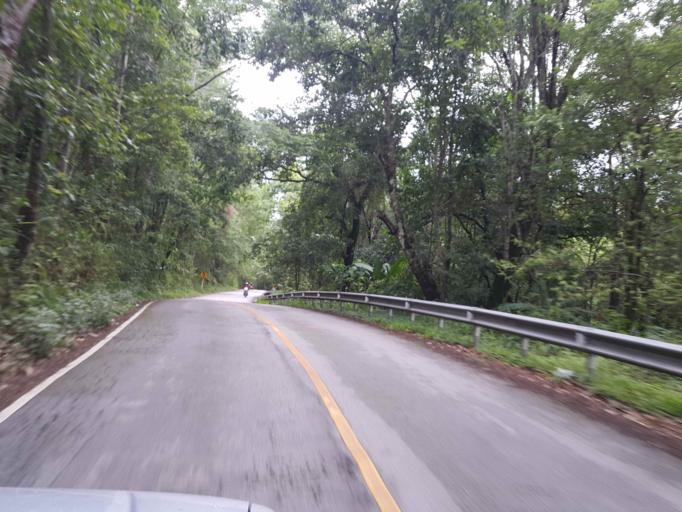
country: TH
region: Chiang Mai
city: Mae Chaem
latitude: 18.5135
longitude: 98.4566
